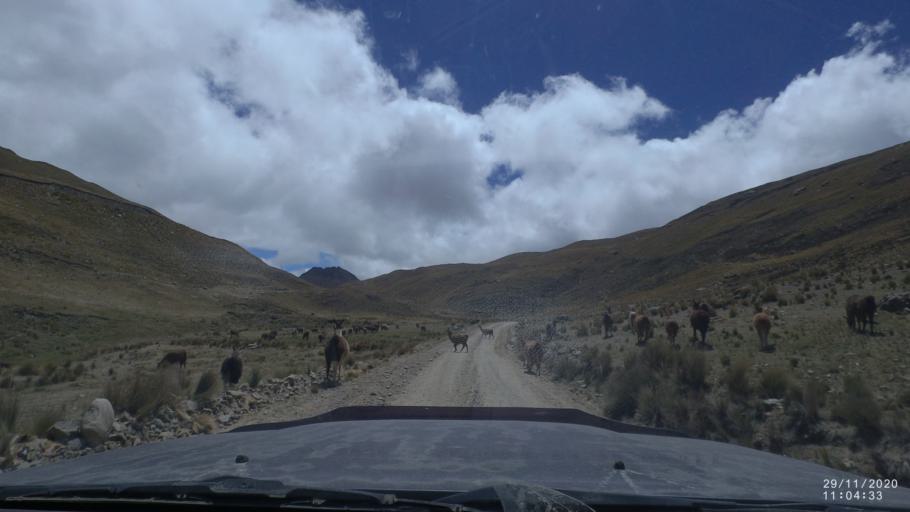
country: BO
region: Cochabamba
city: Cochabamba
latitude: -17.1881
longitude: -66.2159
